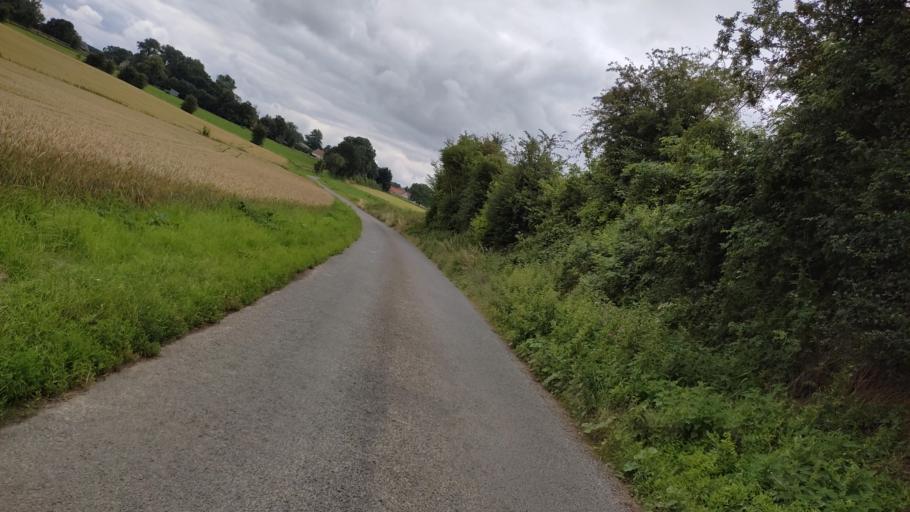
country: FR
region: Nord-Pas-de-Calais
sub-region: Departement du Pas-de-Calais
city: Beaumetz-les-Loges
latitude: 50.2459
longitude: 2.6333
